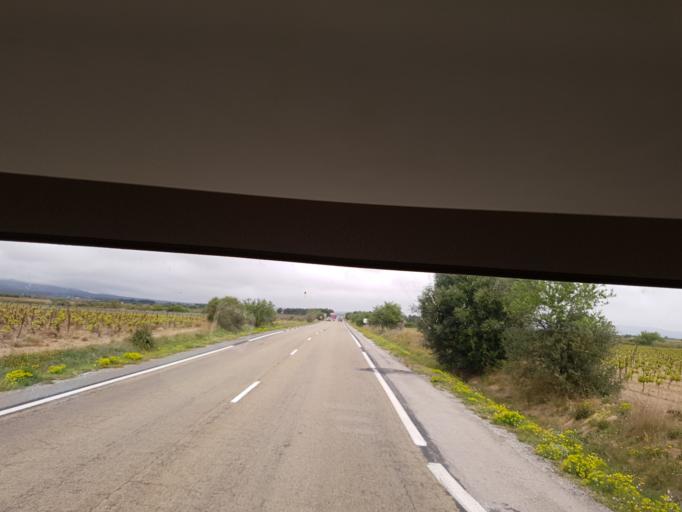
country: FR
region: Languedoc-Roussillon
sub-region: Departement de l'Aude
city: Leucate
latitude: 42.9250
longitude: 2.9947
